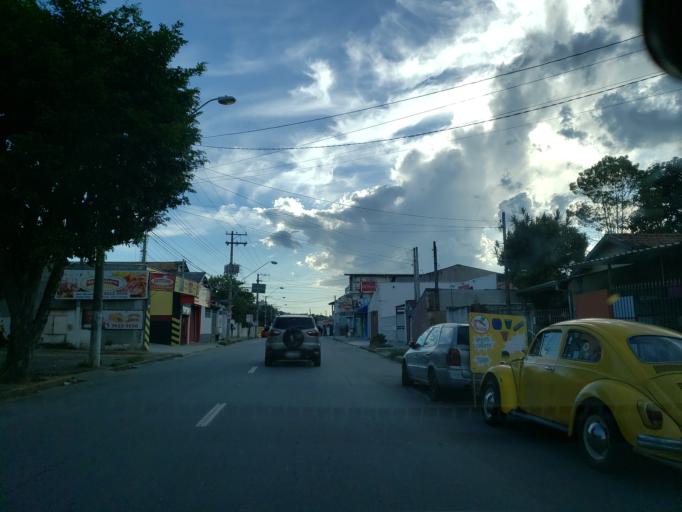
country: BR
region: Sao Paulo
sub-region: Taubate
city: Taubate
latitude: -23.0370
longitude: -45.5675
